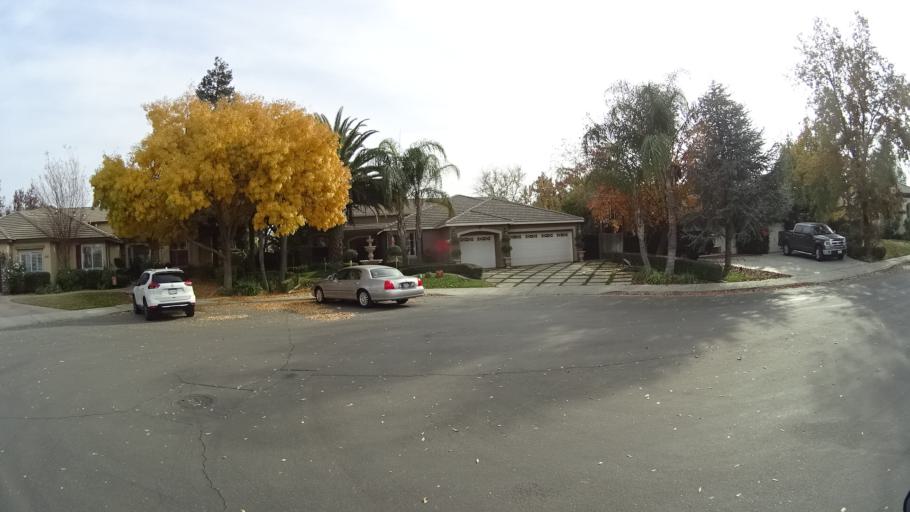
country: US
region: California
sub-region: Kern County
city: Rosedale
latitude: 35.3445
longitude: -119.1403
